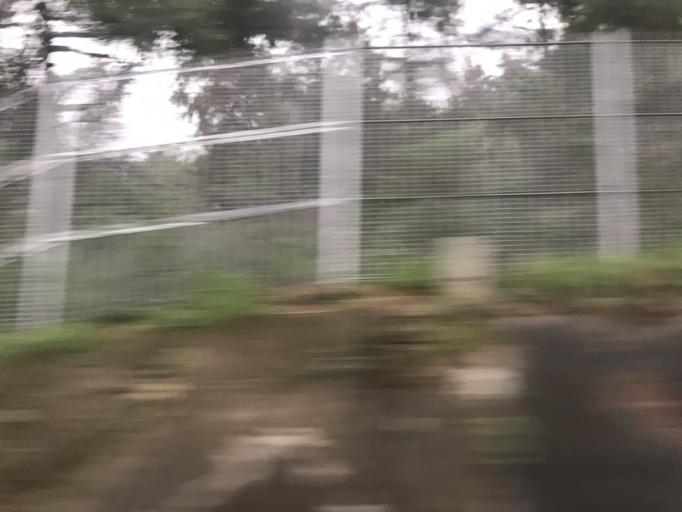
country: HK
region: Sha Tin
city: Sha Tin
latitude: 22.4050
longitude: 114.2067
